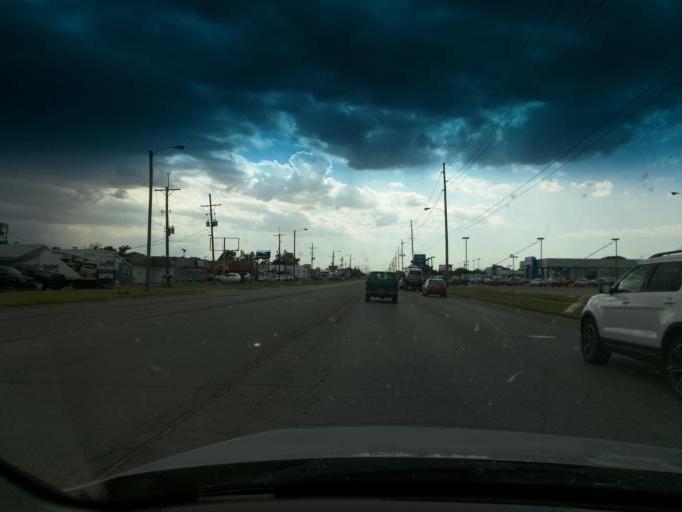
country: US
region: Kansas
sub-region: Reno County
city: Hutchinson
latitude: 38.0866
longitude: -97.9051
